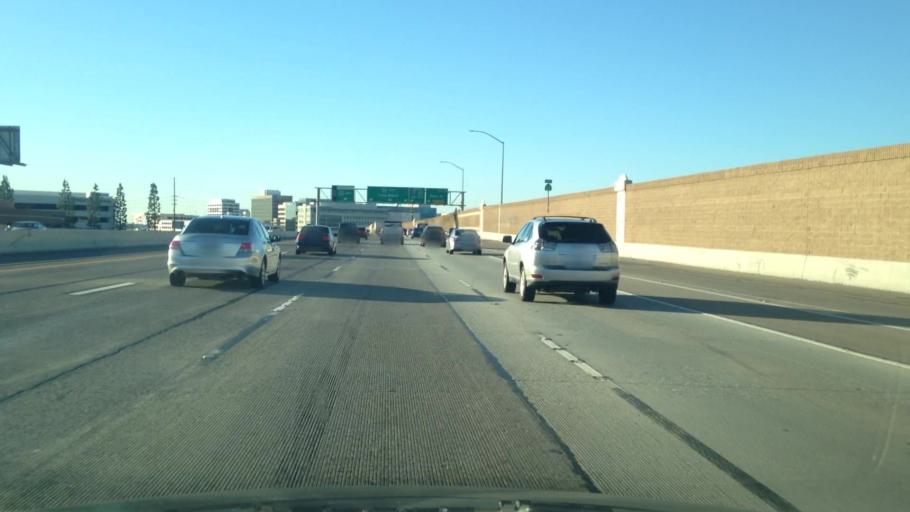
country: US
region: California
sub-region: Orange County
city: Orange
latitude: 33.7769
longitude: -117.8560
